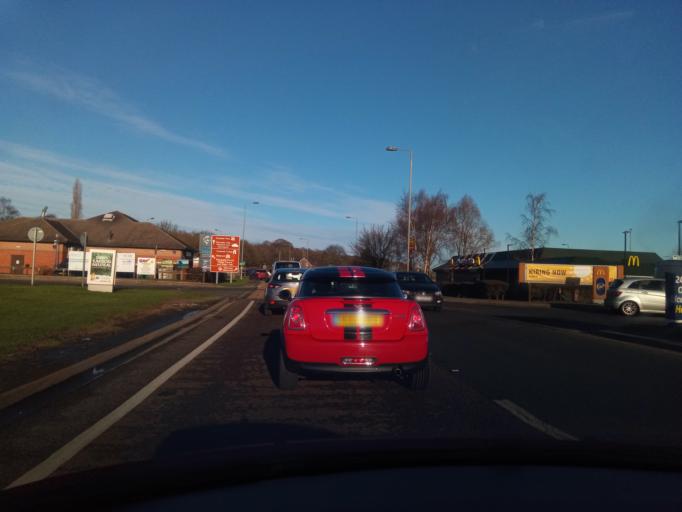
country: GB
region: England
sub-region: Nottinghamshire
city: Edwinstowe
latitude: 53.2000
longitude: -1.0268
